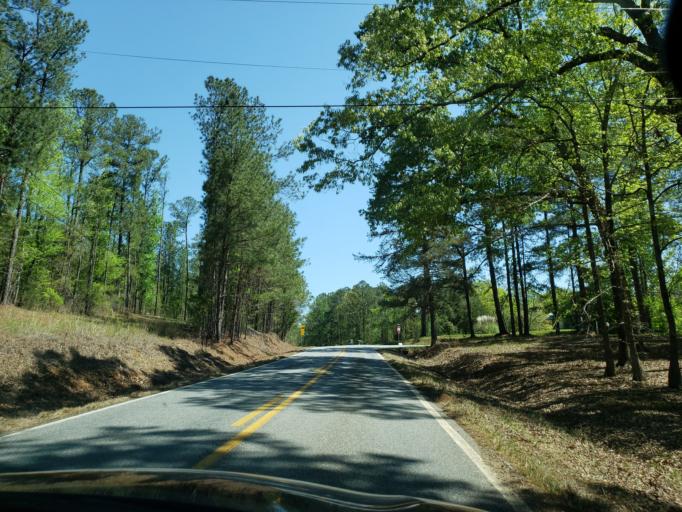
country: US
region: Alabama
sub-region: Elmore County
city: Tallassee
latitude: 32.6863
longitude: -85.8670
